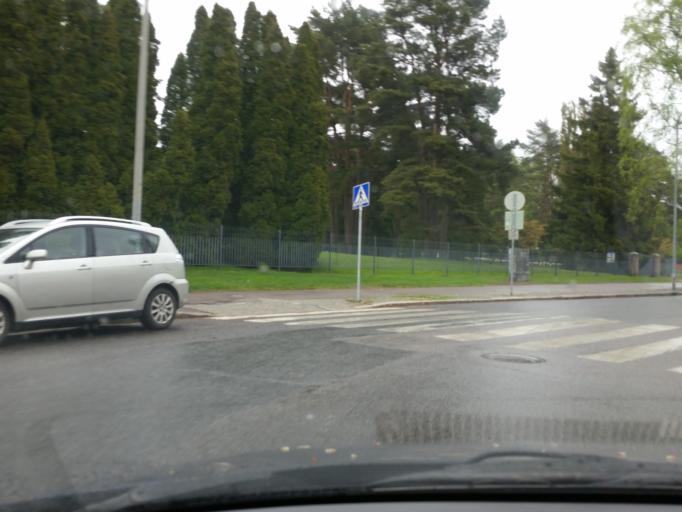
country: FI
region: Uusimaa
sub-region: Helsinki
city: Helsinki
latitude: 60.1731
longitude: 24.9099
